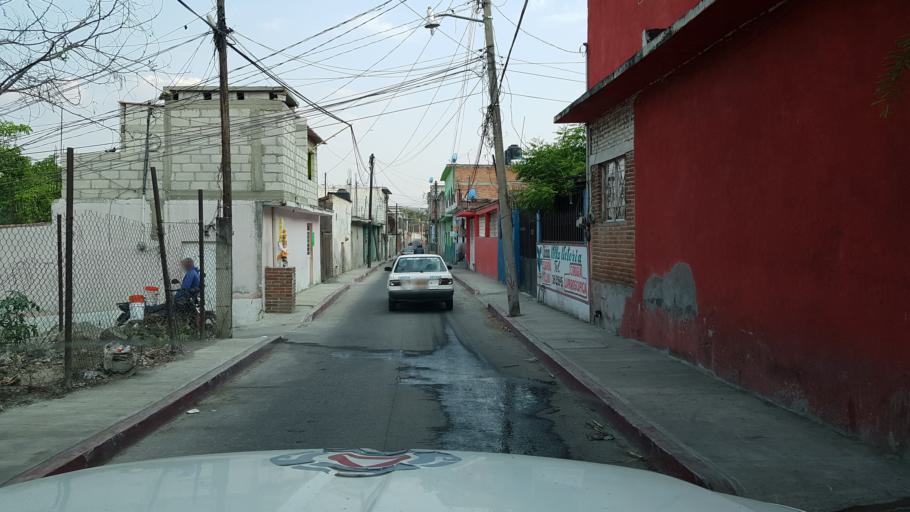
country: MX
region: Morelos
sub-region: Ayala
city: Ciudad Ayala
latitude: 18.7693
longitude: -98.9846
